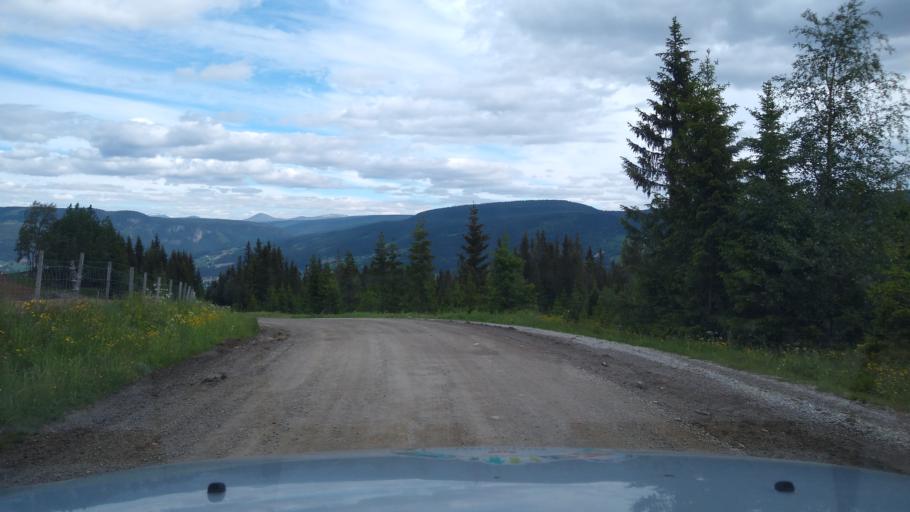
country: NO
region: Oppland
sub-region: Ringebu
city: Ringebu
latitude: 61.4940
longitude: 10.1451
